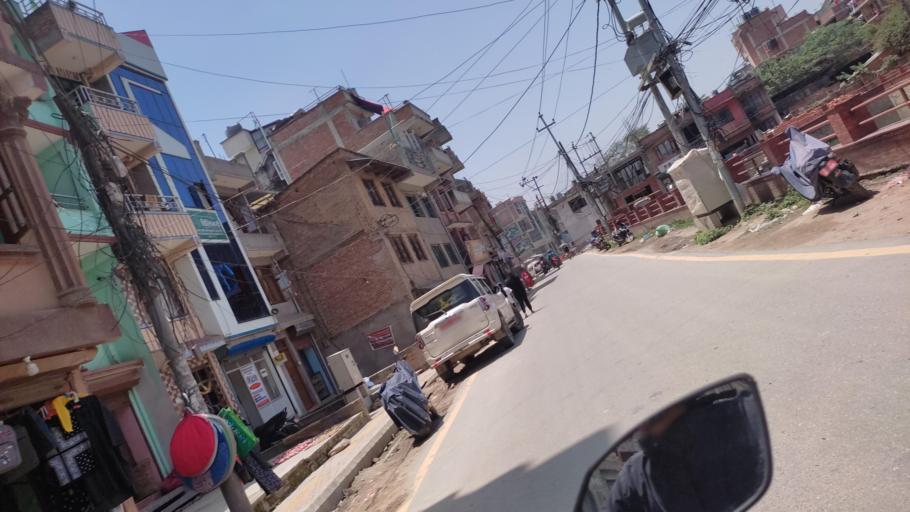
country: NP
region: Central Region
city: Kirtipur
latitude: 27.6777
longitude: 85.2745
